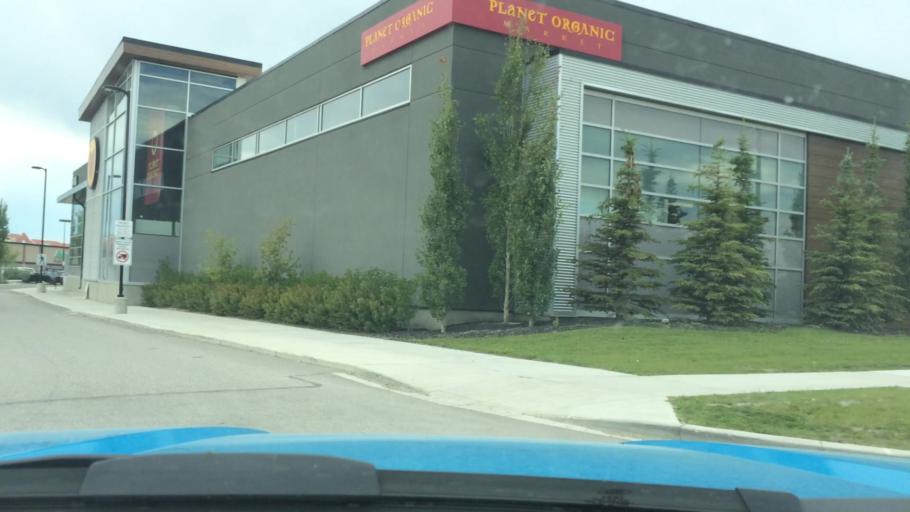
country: CA
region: Alberta
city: Calgary
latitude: 51.1529
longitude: -114.2108
